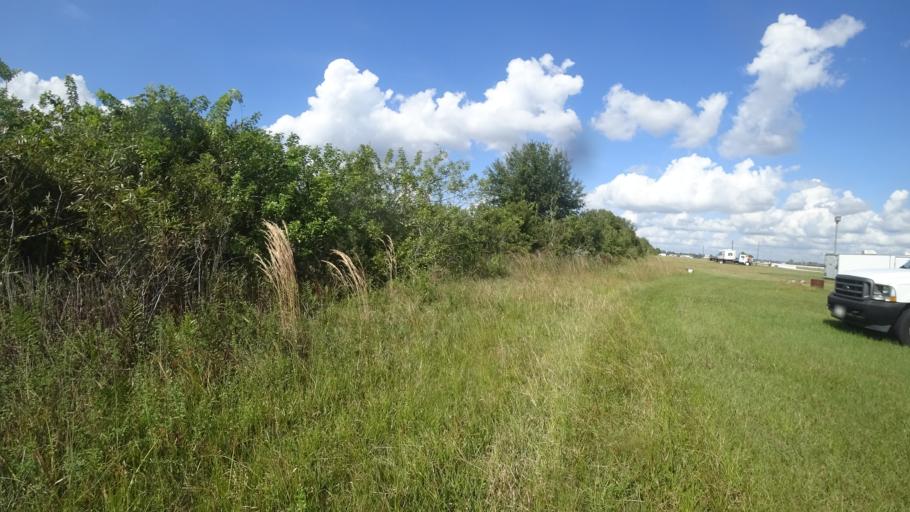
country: US
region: Florida
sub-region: Sarasota County
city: The Meadows
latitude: 27.4653
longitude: -82.3278
